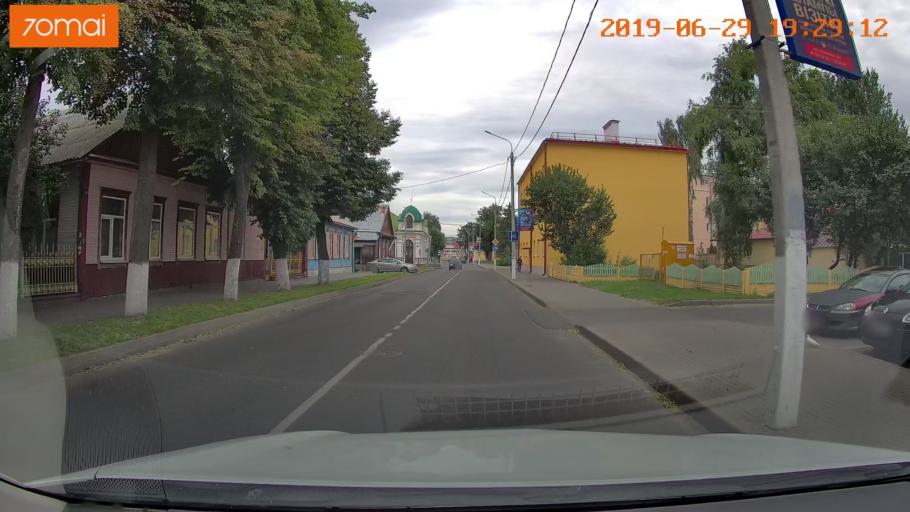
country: BY
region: Brest
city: Pinsk
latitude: 52.1136
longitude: 26.1068
